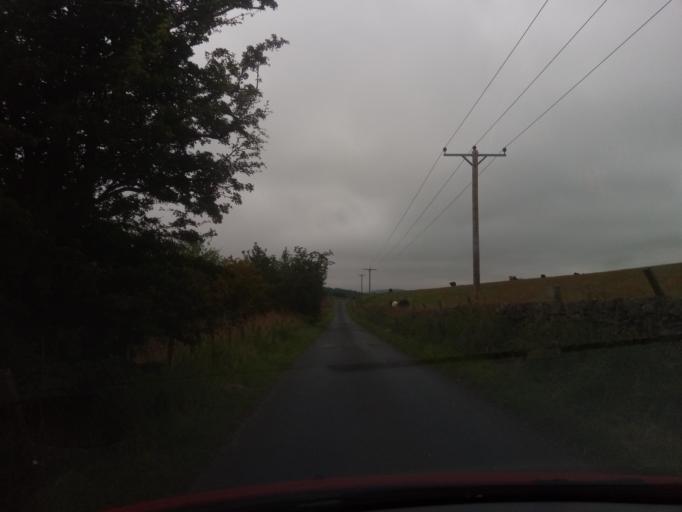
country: GB
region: Scotland
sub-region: The Scottish Borders
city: Galashiels
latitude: 55.6835
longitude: -2.8728
